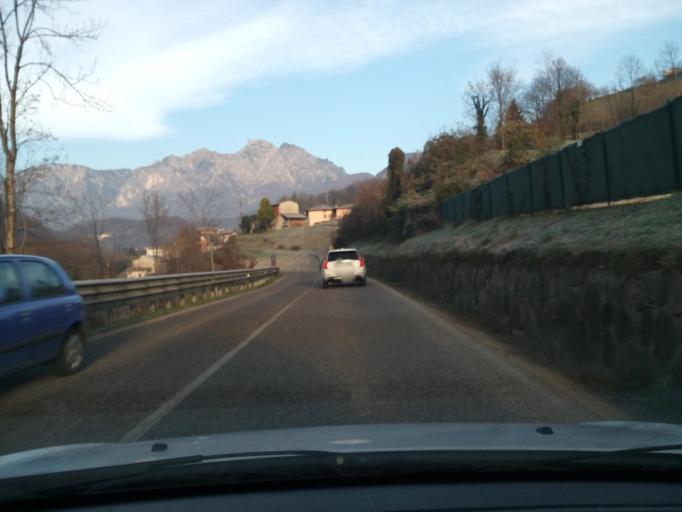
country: IT
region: Veneto
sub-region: Provincia di Vicenza
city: Valli del Pasubio
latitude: 45.7321
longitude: 11.2746
